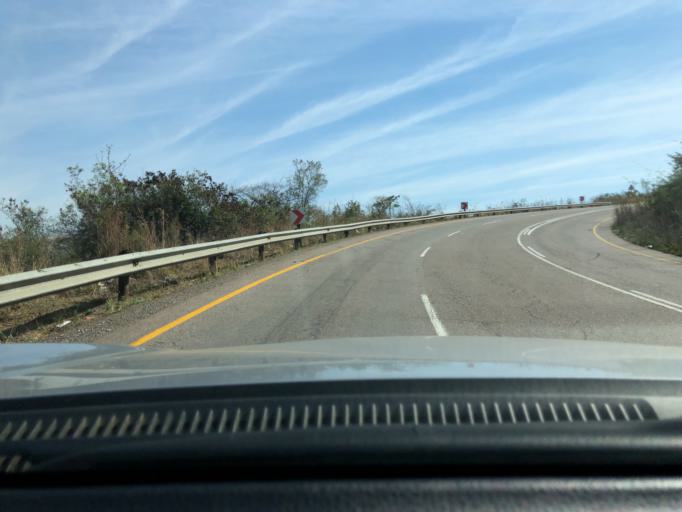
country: ZA
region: KwaZulu-Natal
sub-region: uMgungundlovu District Municipality
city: Richmond
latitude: -29.9997
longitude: 30.2455
